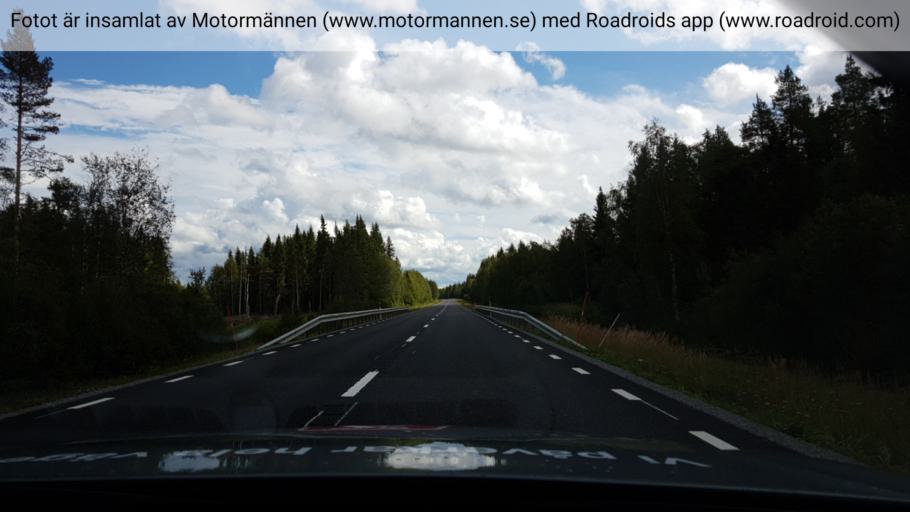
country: SE
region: Jaemtland
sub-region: OEstersunds Kommun
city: Brunflo
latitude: 63.2010
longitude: 14.9378
